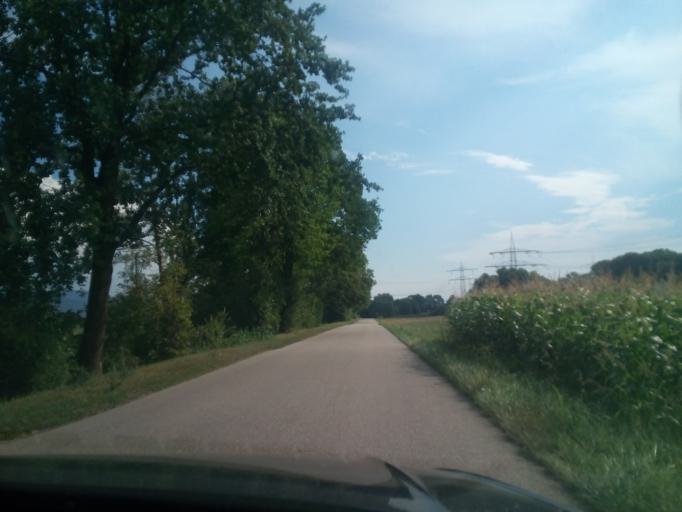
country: DE
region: Baden-Wuerttemberg
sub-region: Karlsruhe Region
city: Ottenhofen
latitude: 48.7536
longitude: 8.1379
